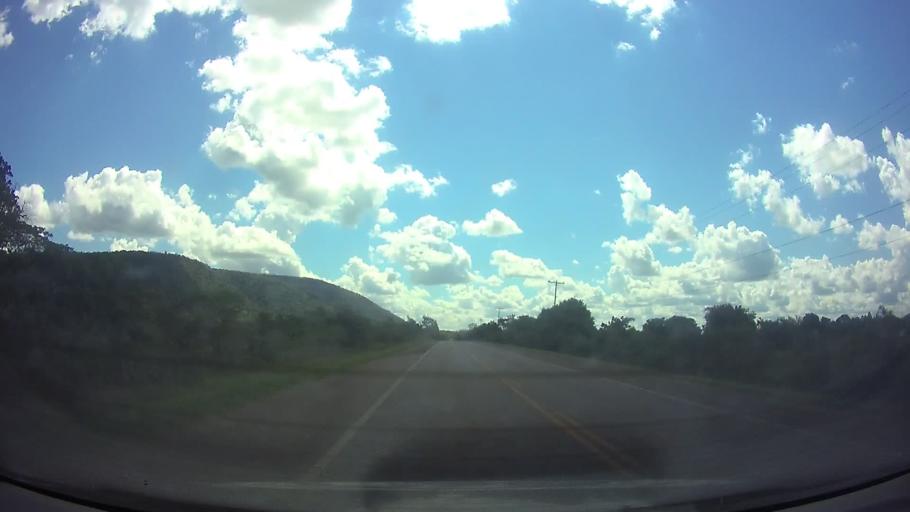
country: PY
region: Paraguari
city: La Colmena
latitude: -25.9188
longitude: -56.7246
